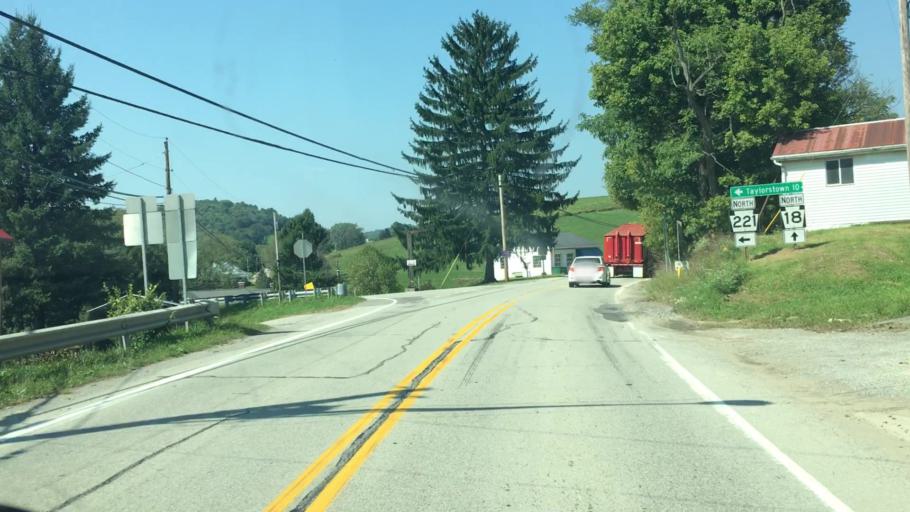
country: US
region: Pennsylvania
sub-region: Washington County
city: Washington
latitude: 40.0472
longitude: -80.2945
